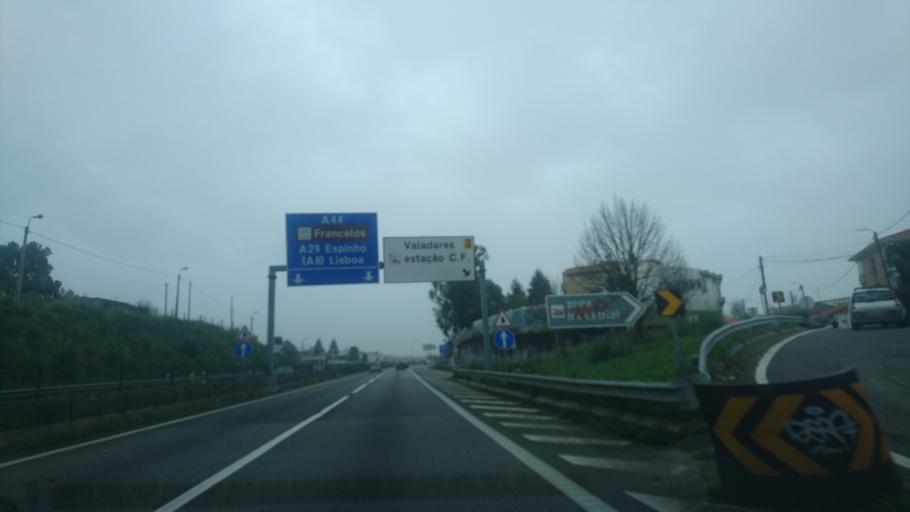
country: PT
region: Porto
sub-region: Vila Nova de Gaia
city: Vilar do Paraiso
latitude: 41.1029
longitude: -8.6265
